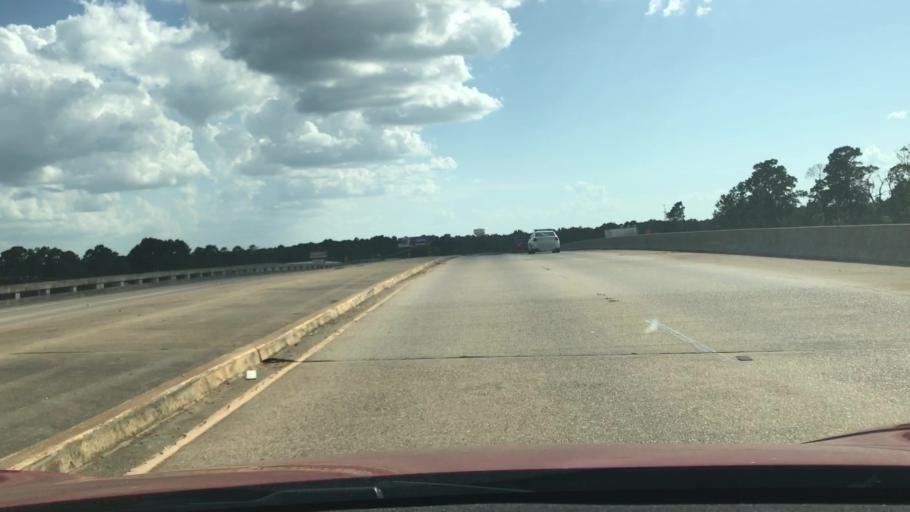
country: US
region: Louisiana
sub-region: Bossier Parish
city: Bossier City
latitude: 32.4012
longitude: -93.7355
